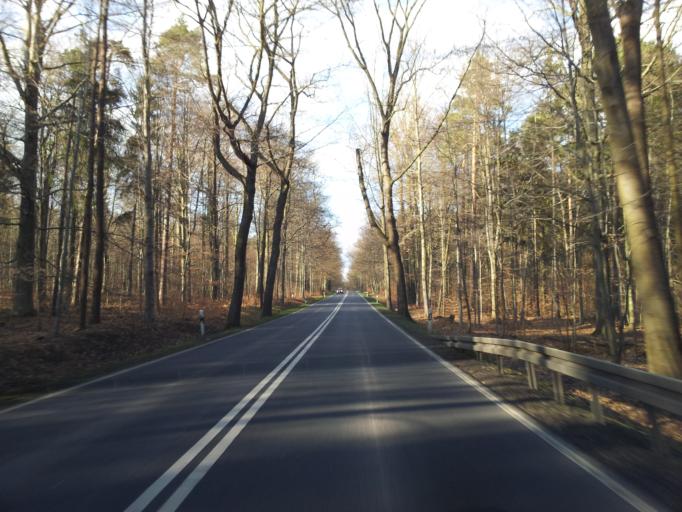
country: DE
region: Saxony
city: Ottendorf-Okrilla
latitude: 51.2120
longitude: 13.8401
